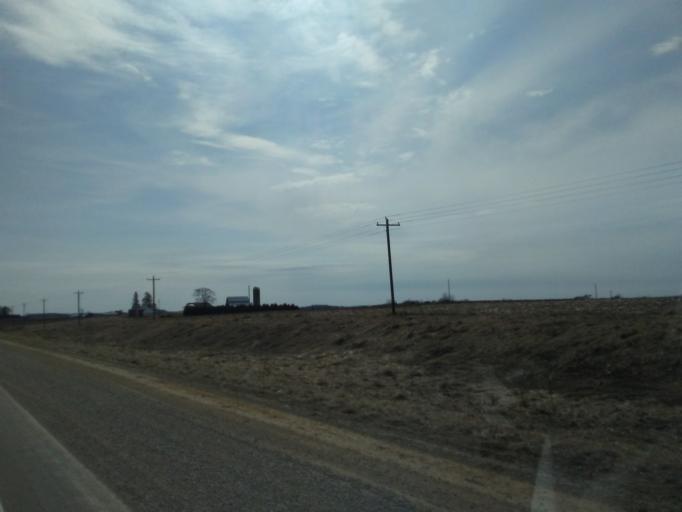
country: US
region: Iowa
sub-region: Winneshiek County
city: Decorah
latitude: 43.4414
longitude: -91.8617
